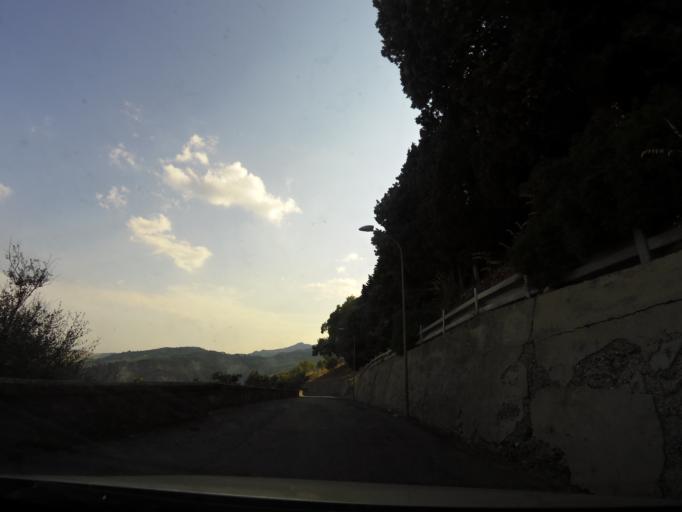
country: IT
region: Calabria
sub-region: Provincia di Reggio Calabria
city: Stilo
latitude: 38.4785
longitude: 16.4666
